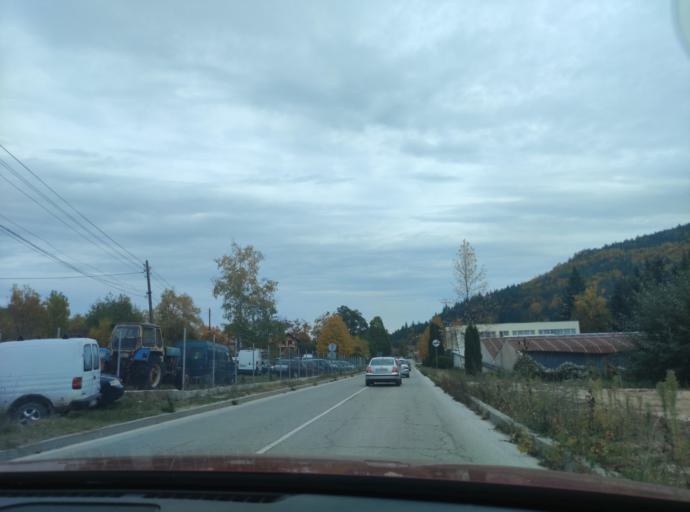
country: BG
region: Montana
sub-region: Obshtina Berkovitsa
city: Berkovitsa
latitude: 43.1887
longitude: 23.1581
